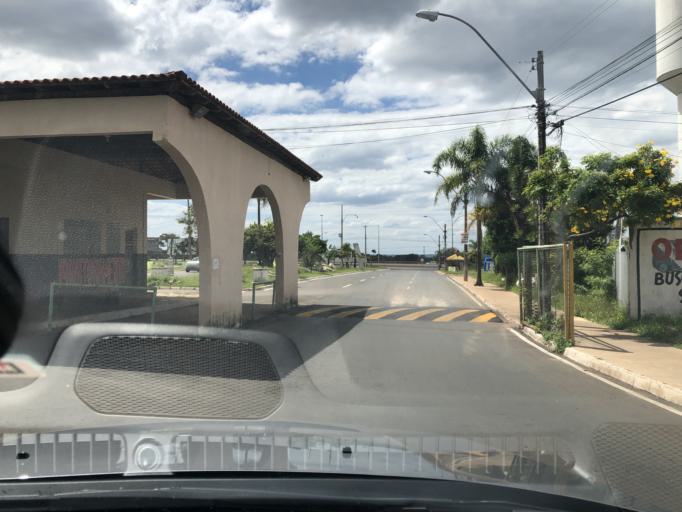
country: BR
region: Federal District
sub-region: Brasilia
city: Brasilia
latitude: -15.9922
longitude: -47.9879
